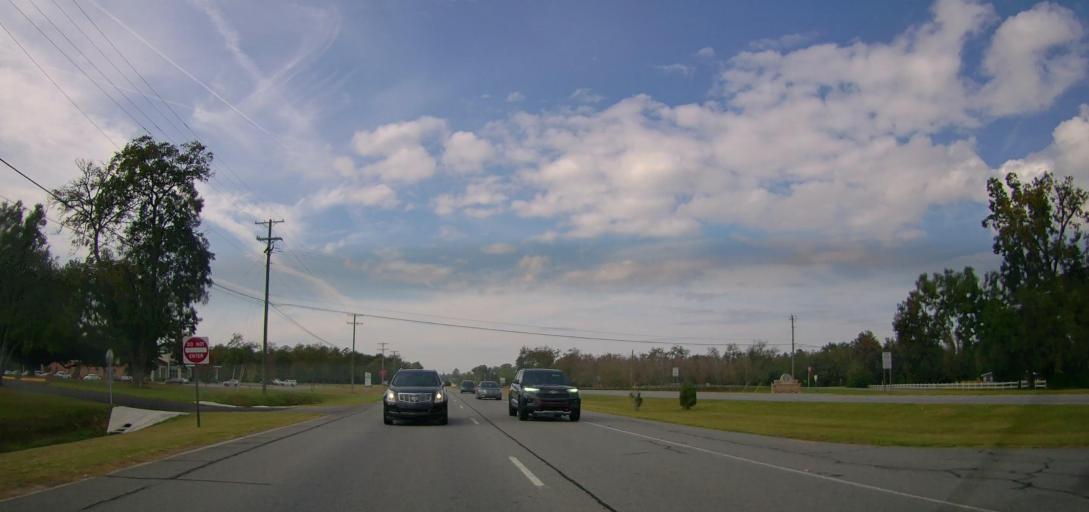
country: US
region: Georgia
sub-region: Mitchell County
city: Camilla
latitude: 31.2183
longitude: -84.1871
